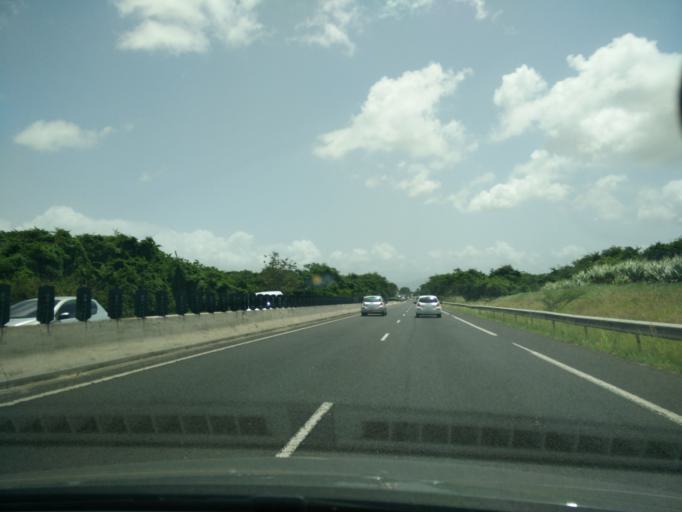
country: GP
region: Guadeloupe
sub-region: Guadeloupe
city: Baie-Mahault
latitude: 16.2664
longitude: -61.5627
